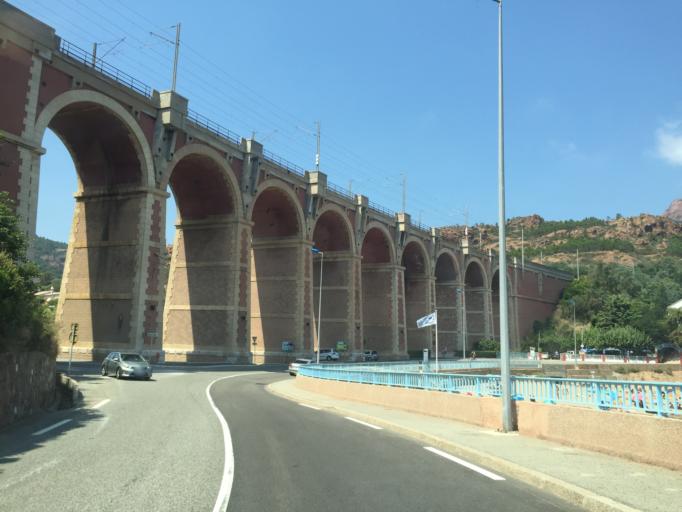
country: FR
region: Provence-Alpes-Cote d'Azur
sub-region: Departement des Alpes-Maritimes
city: Theoule-sur-Mer
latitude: 43.4368
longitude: 6.8923
